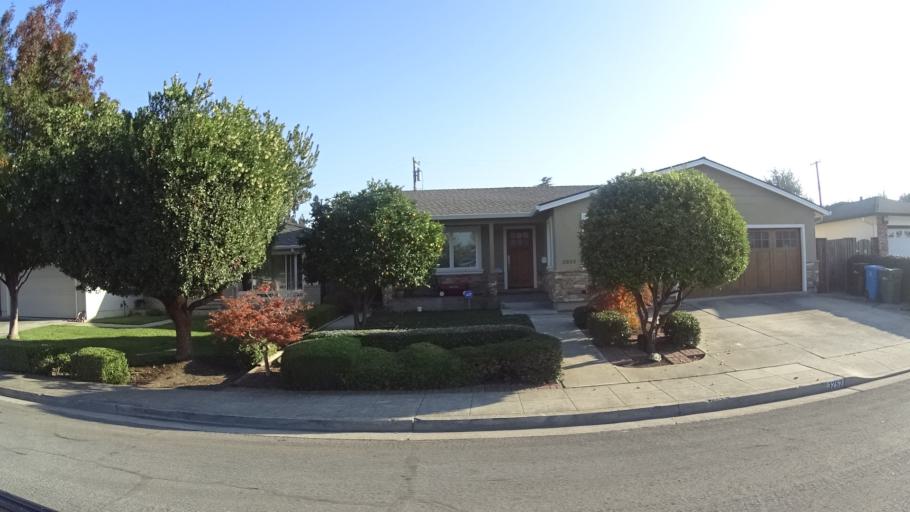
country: US
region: California
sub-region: Santa Clara County
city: Santa Clara
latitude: 37.3445
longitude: -121.9852
